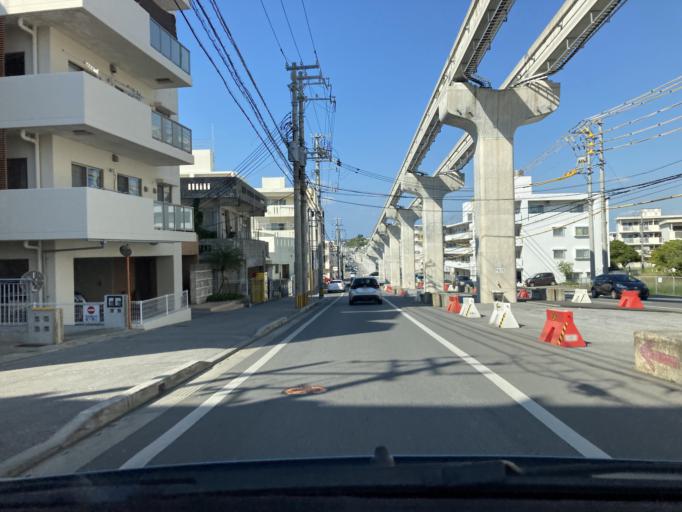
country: JP
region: Okinawa
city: Ginowan
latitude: 26.2280
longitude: 127.7291
